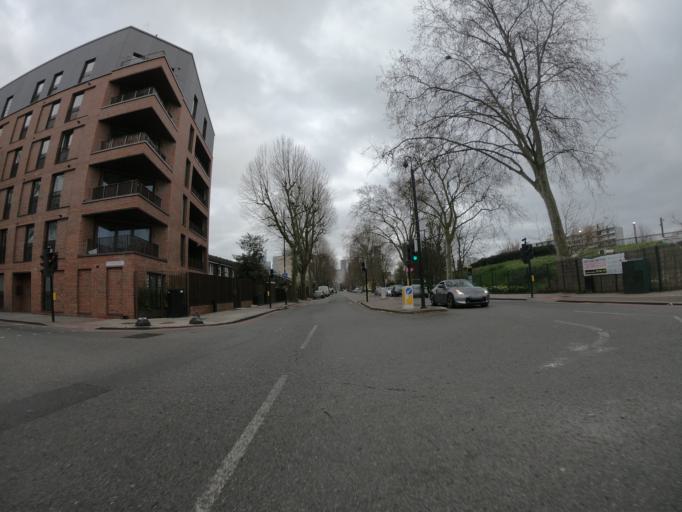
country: GB
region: England
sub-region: Greater London
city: Poplar
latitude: 51.5173
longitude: -0.0297
